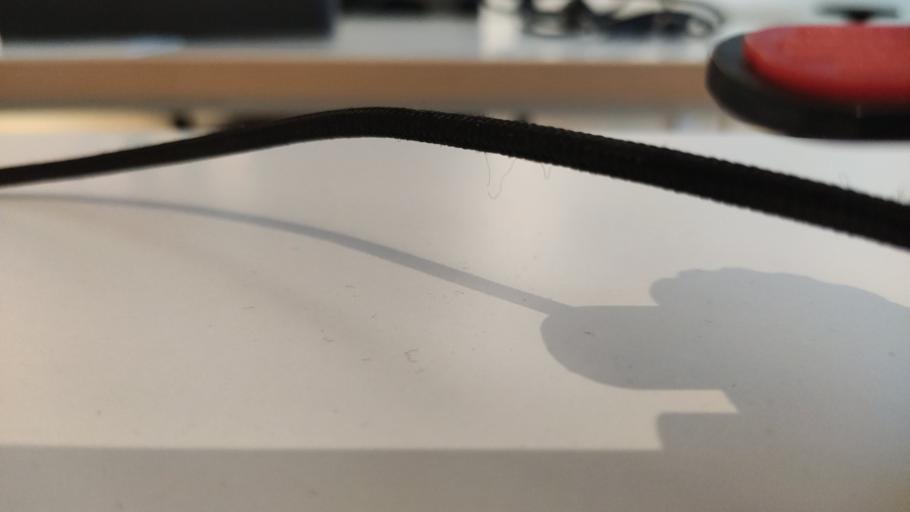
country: RU
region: Moskovskaya
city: Novopetrovskoye
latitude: 55.8705
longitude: 36.3988
